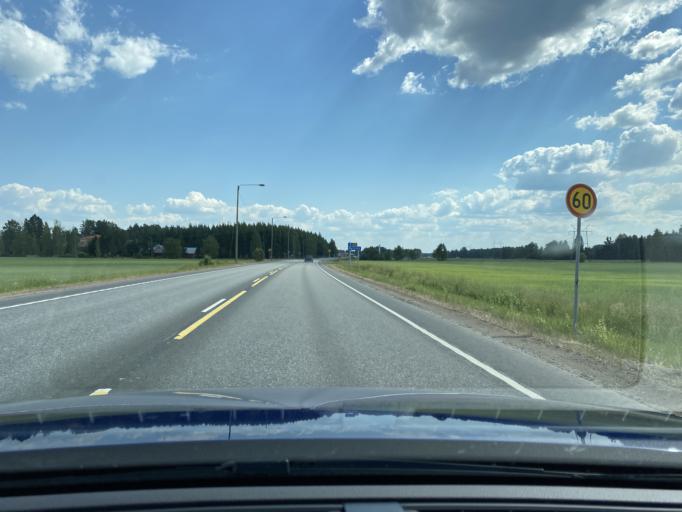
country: FI
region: Satakunta
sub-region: Rauma
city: Eura
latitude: 61.1386
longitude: 22.1173
